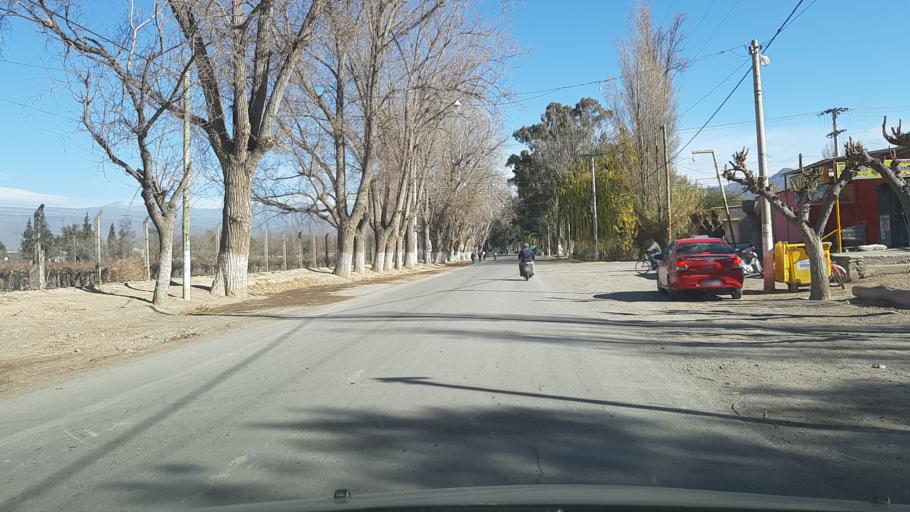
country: AR
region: San Juan
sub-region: Departamento de Zonda
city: Zonda
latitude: -31.4612
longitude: -68.7330
